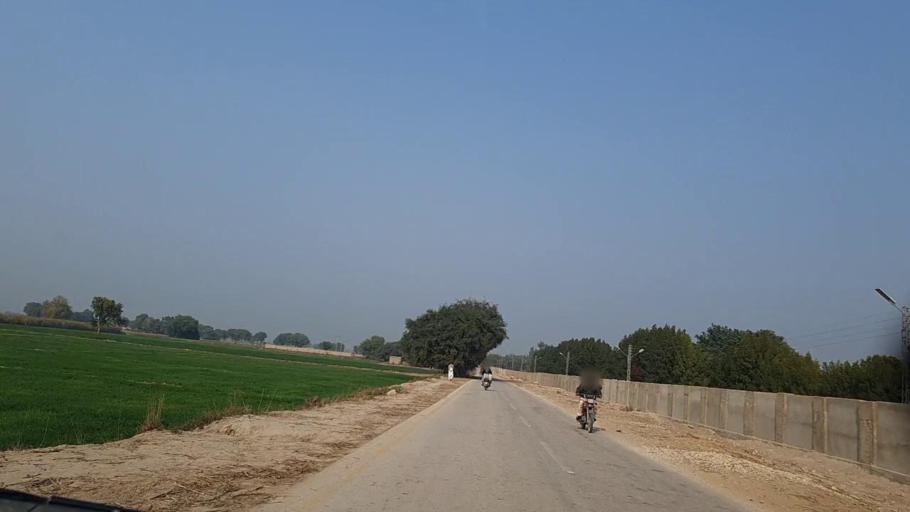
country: PK
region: Sindh
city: Sann
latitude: 26.1783
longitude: 68.1081
